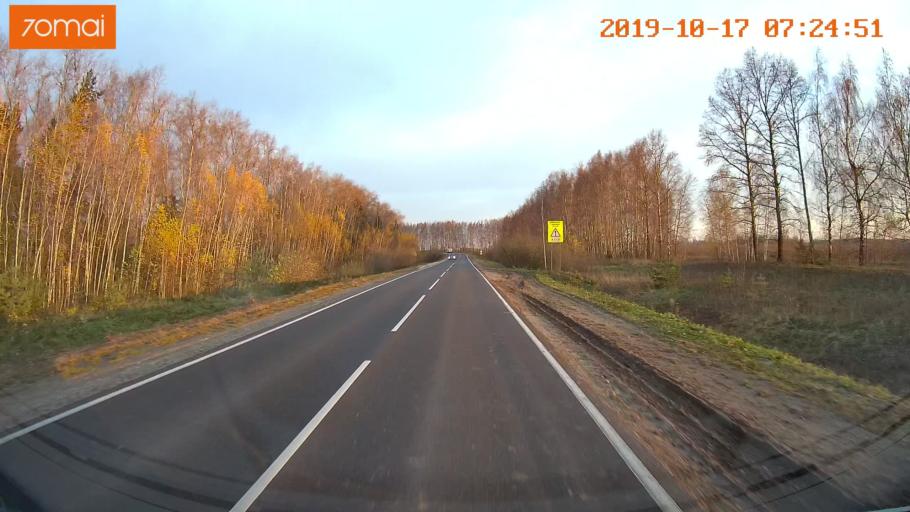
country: RU
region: Ivanovo
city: Gavrilov Posad
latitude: 56.3438
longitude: 40.1120
